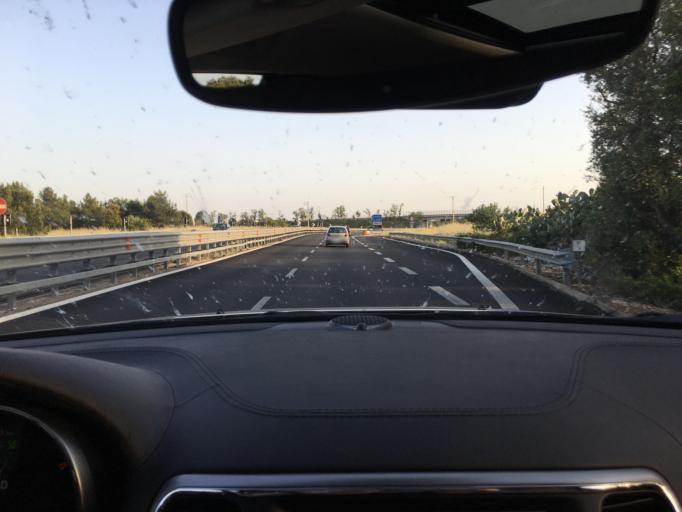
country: IT
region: Apulia
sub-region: Provincia di Lecce
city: Lequile
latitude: 40.2923
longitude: 18.1329
